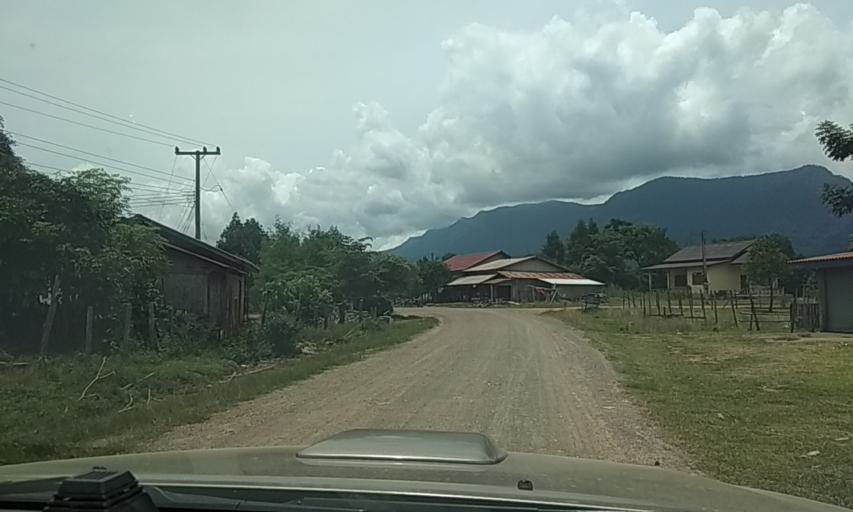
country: LA
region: Bolikhamxai
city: Ban Nahin
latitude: 18.1410
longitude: 104.7578
